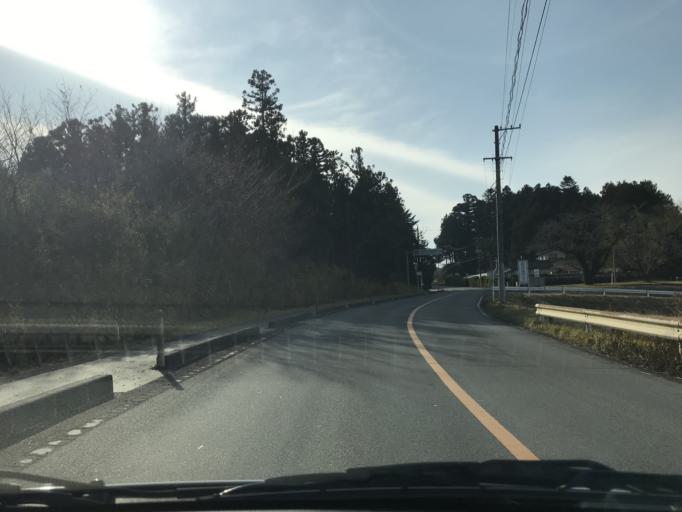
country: JP
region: Miyagi
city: Wakuya
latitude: 38.6901
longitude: 141.1389
